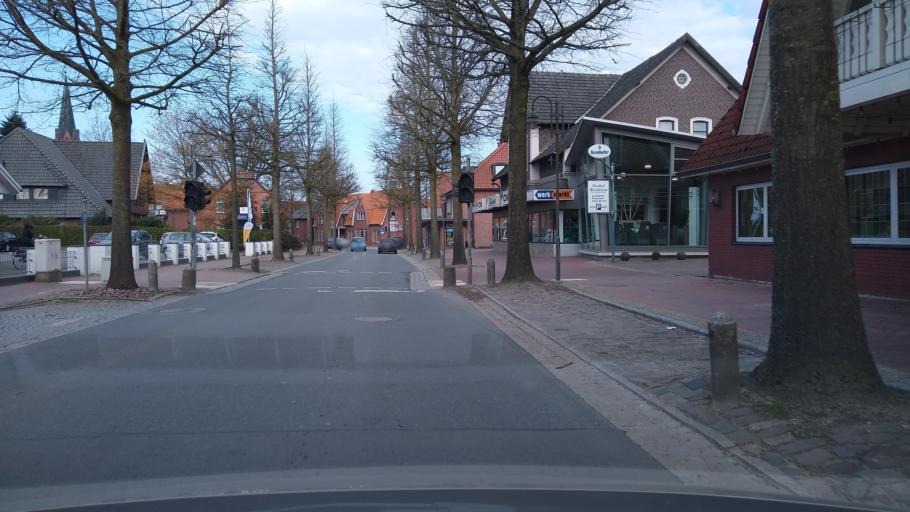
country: DE
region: Lower Saxony
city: Emstek
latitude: 52.8339
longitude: 8.1587
